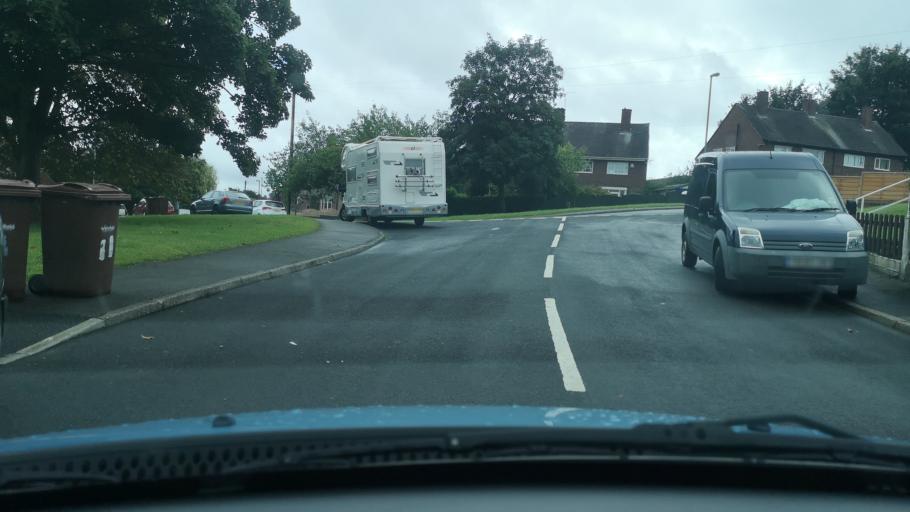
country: GB
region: England
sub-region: City and Borough of Wakefield
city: Low Ackworth
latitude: 53.6459
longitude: -1.3370
